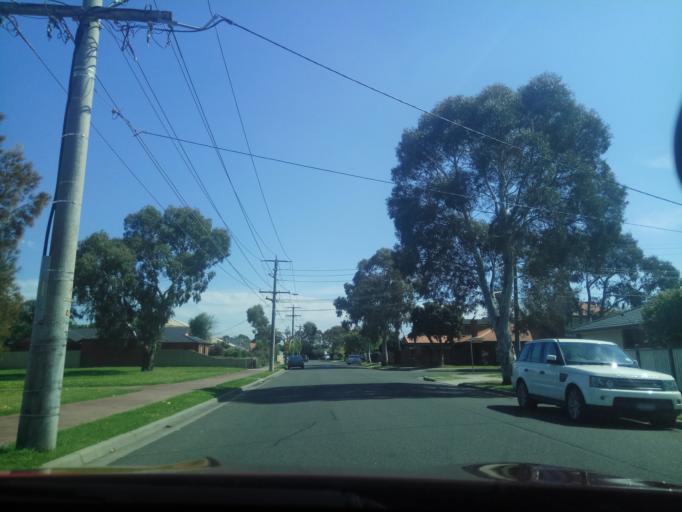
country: AU
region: Victoria
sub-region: Kingston
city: Aspendale Gardens
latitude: -38.0201
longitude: 145.1108
